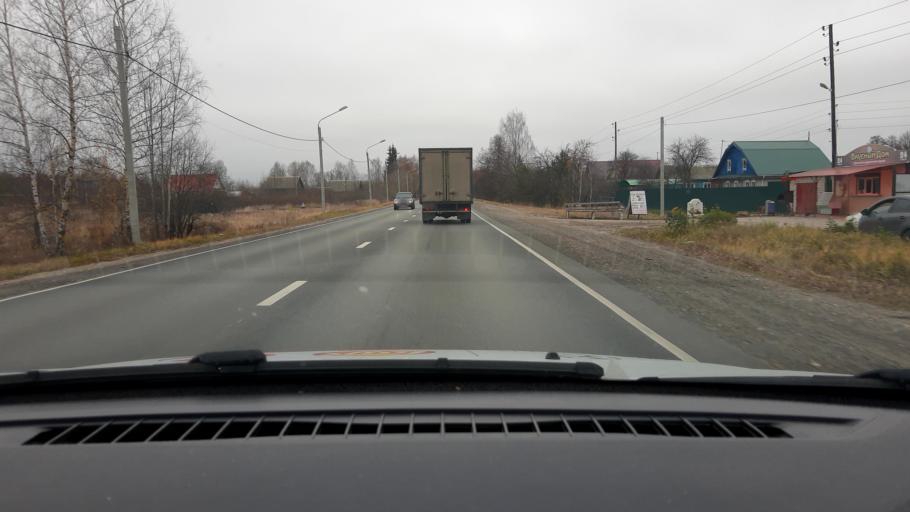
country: RU
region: Nizjnij Novgorod
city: Gorodets
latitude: 56.6045
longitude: 43.4485
